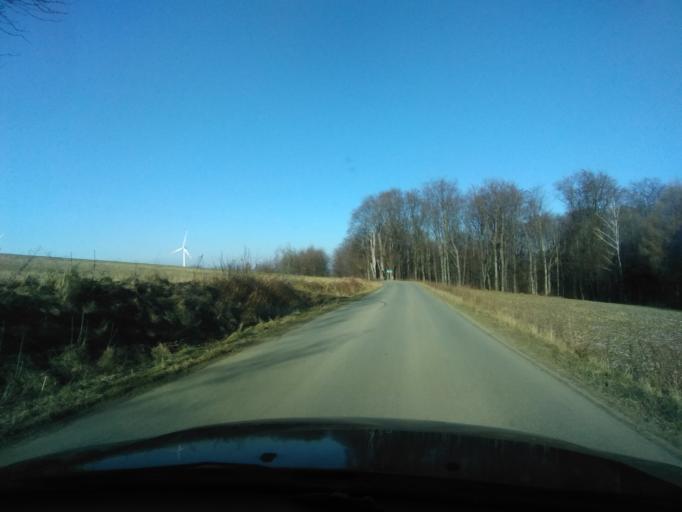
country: PL
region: Subcarpathian Voivodeship
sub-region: Powiat krosnienski
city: Rymanow
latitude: 49.5922
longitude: 21.8935
